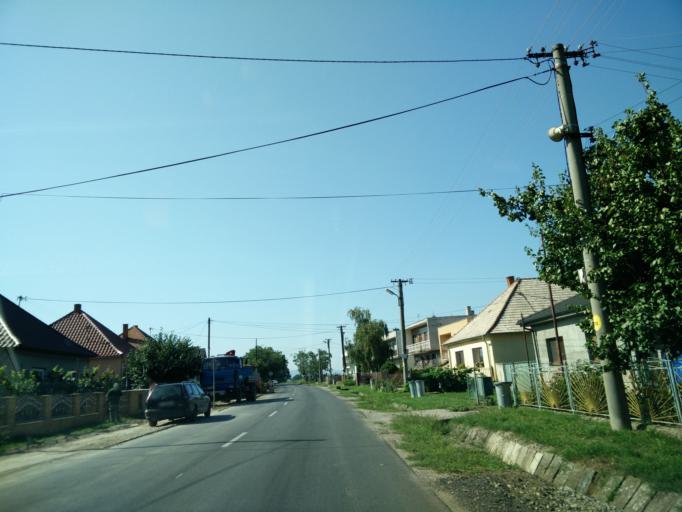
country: SK
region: Nitriansky
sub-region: Okres Nitra
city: Nitra
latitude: 48.4643
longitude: 18.1441
